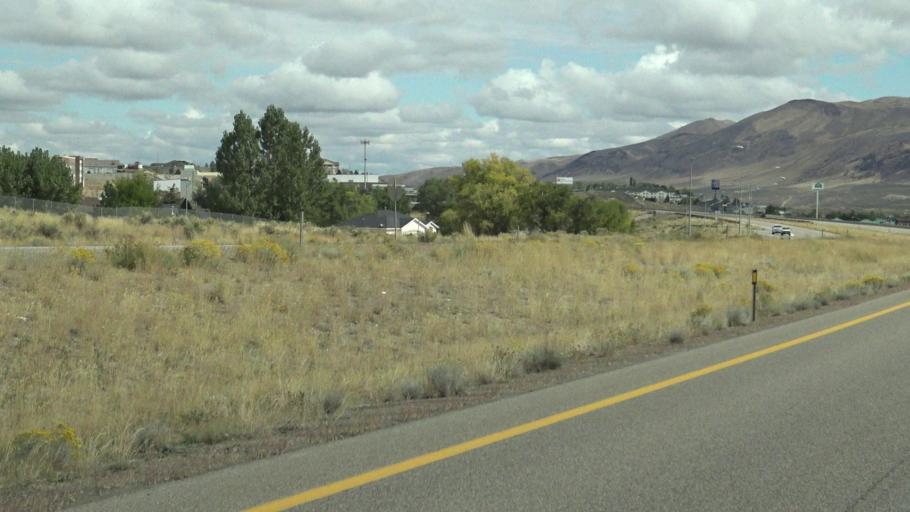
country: US
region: Nevada
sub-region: Elko County
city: Elko
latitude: 40.8483
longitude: -115.7559
